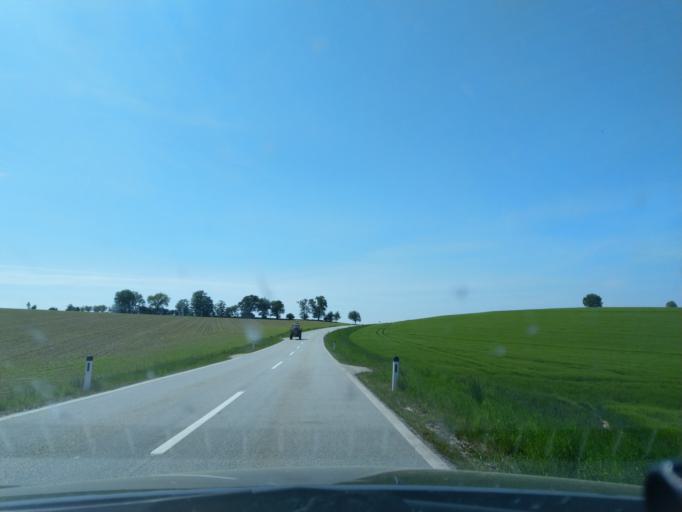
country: DE
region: Bavaria
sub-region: Lower Bavaria
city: Bad Fussing
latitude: 48.2683
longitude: 13.3469
